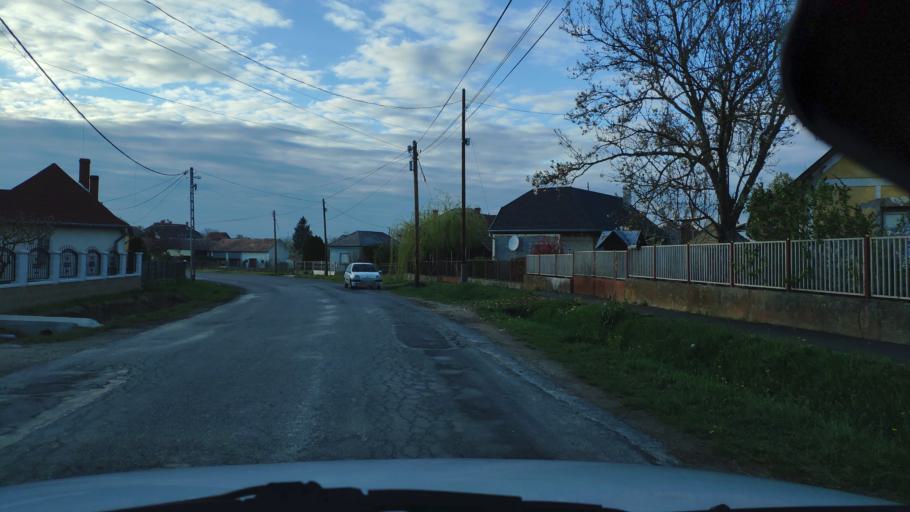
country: HU
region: Zala
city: Nagykanizsa
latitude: 46.4314
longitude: 17.0613
